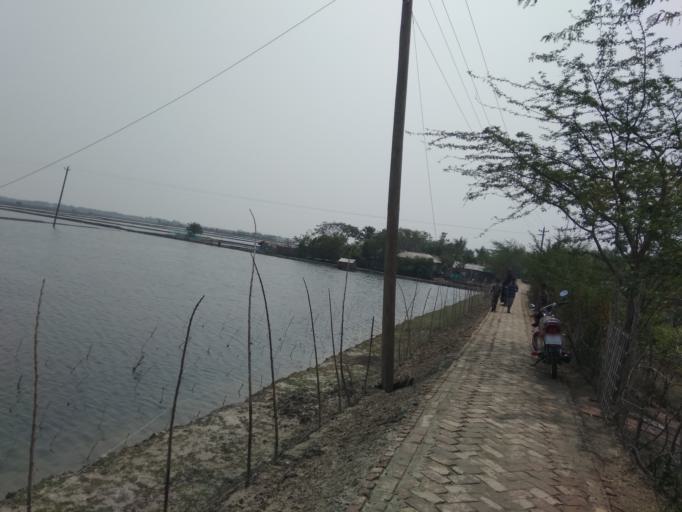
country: IN
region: West Bengal
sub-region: North 24 Parganas
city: Taki
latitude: 22.2802
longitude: 89.2946
